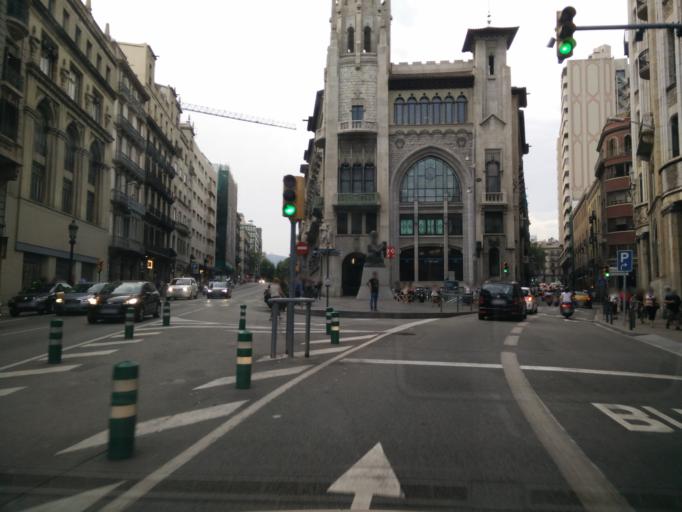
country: ES
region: Catalonia
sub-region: Provincia de Barcelona
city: Ciutat Vella
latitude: 41.3872
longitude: 2.1746
